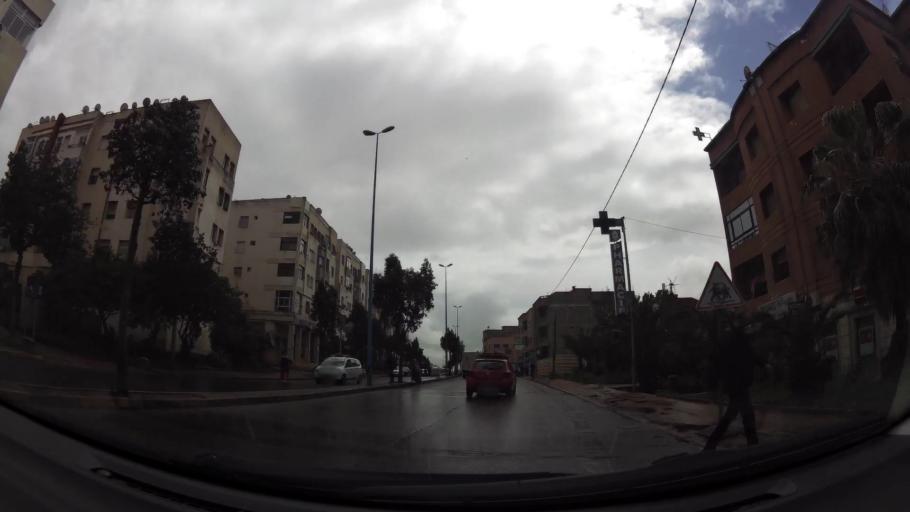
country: MA
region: Grand Casablanca
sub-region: Casablanca
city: Casablanca
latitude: 33.5315
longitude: -7.6481
